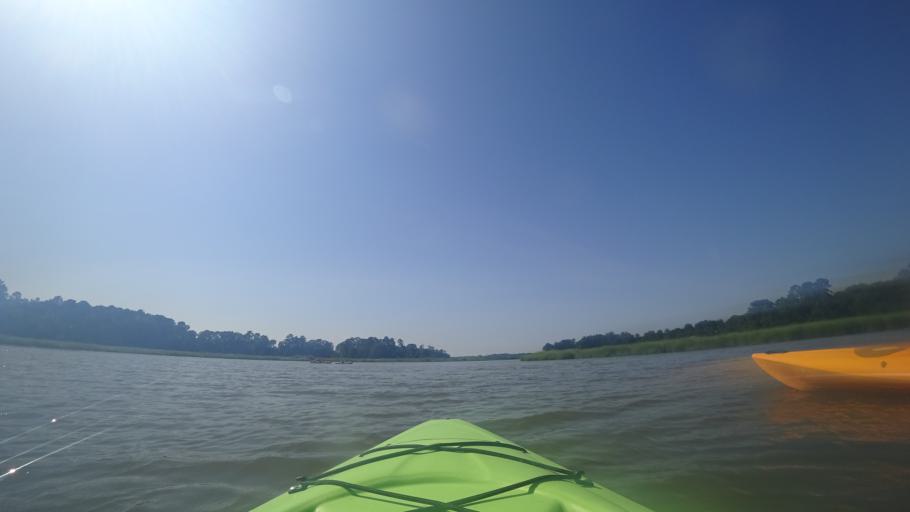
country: US
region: Virginia
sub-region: Isle of Wight County
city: Smithfield
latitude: 36.9708
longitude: -76.6180
